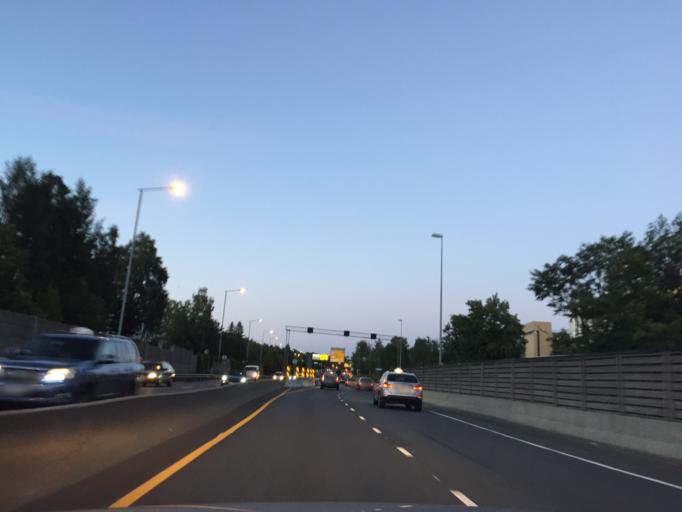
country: NO
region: Oslo
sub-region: Oslo
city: Sjolyststranda
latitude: 59.9342
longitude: 10.6743
